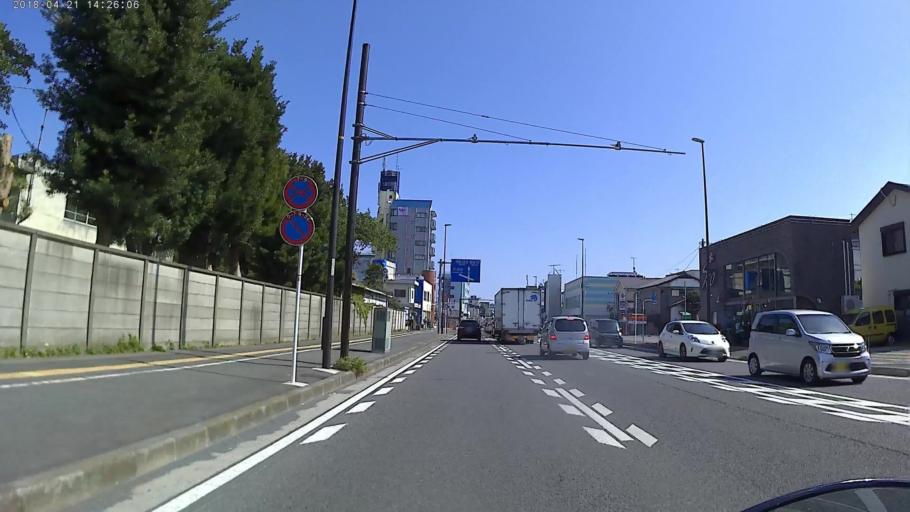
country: JP
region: Kanagawa
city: Hiratsuka
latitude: 35.3378
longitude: 139.3374
